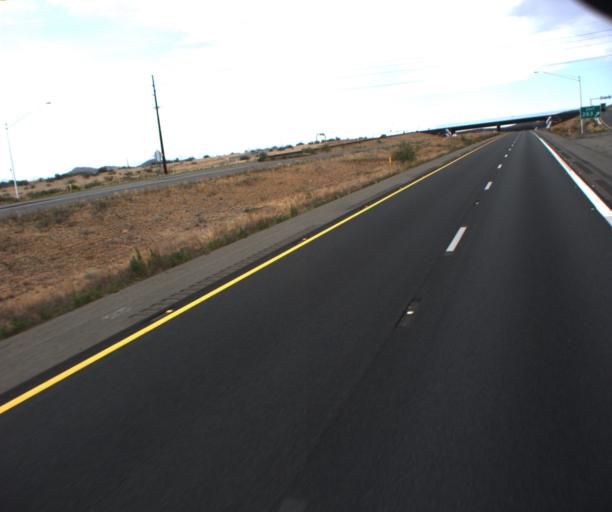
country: US
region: Arizona
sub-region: Yavapai County
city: Cordes Lakes
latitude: 34.3380
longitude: -112.1191
